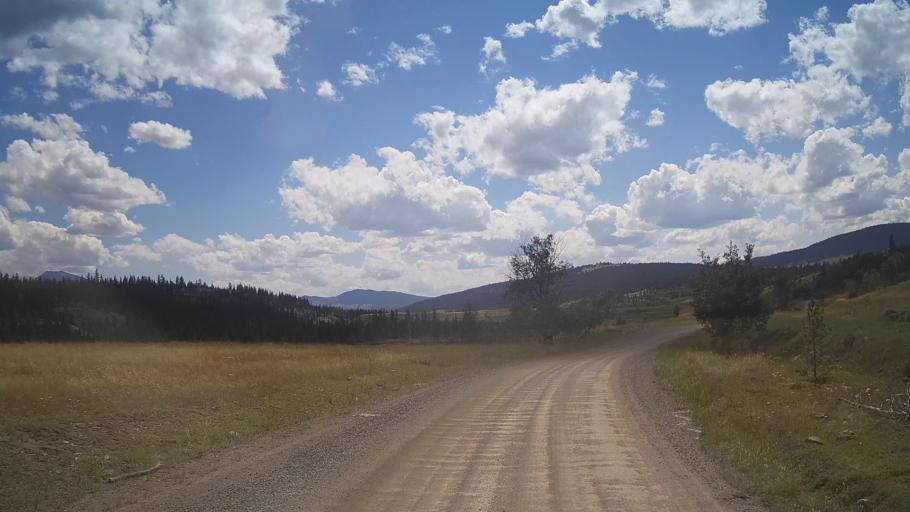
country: CA
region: British Columbia
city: Lillooet
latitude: 51.3291
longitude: -121.9752
